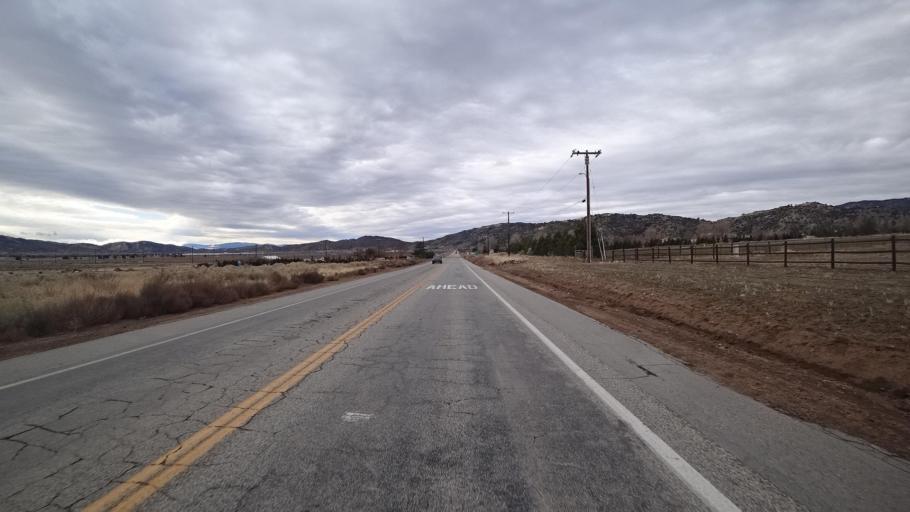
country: US
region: California
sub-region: Kern County
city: Bear Valley Springs
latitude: 35.1306
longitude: -118.5718
